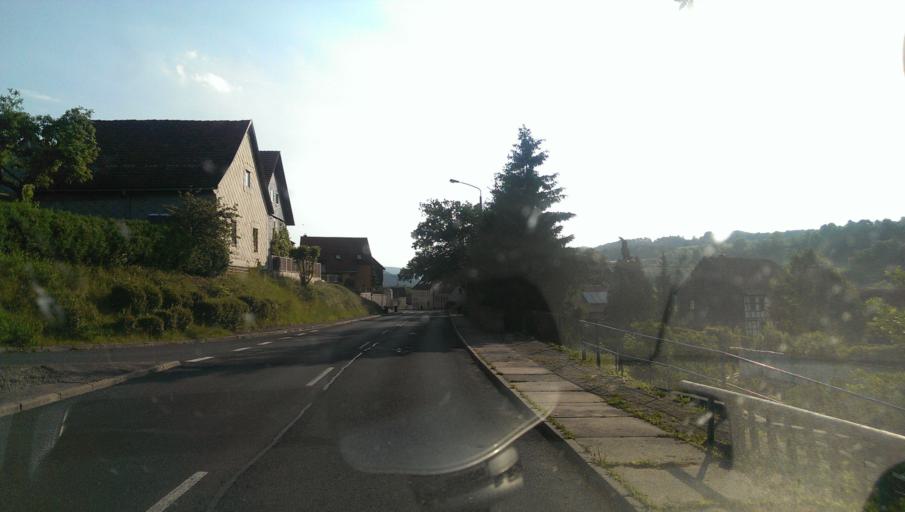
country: DE
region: Thuringia
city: Dillstadt
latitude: 50.5823
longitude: 10.5342
